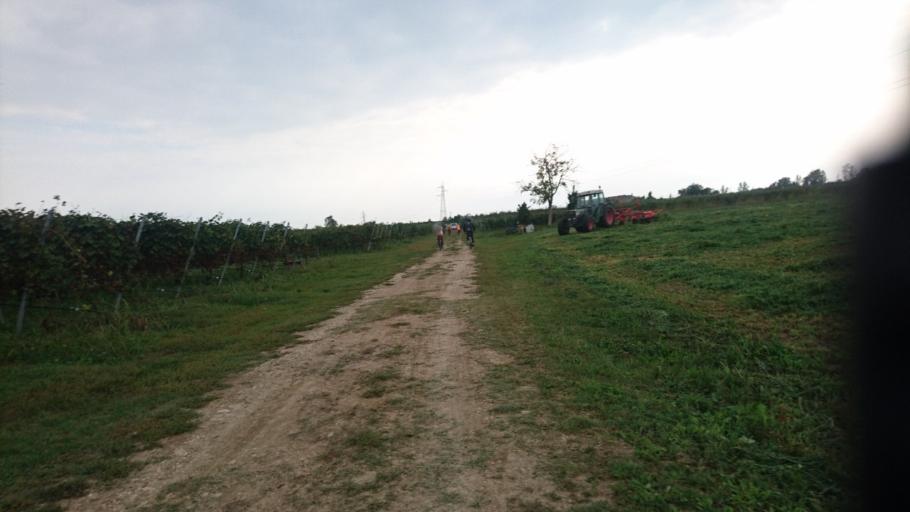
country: IT
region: Veneto
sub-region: Provincia di Verona
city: Caldierino-Rota
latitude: 45.4006
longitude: 11.1381
